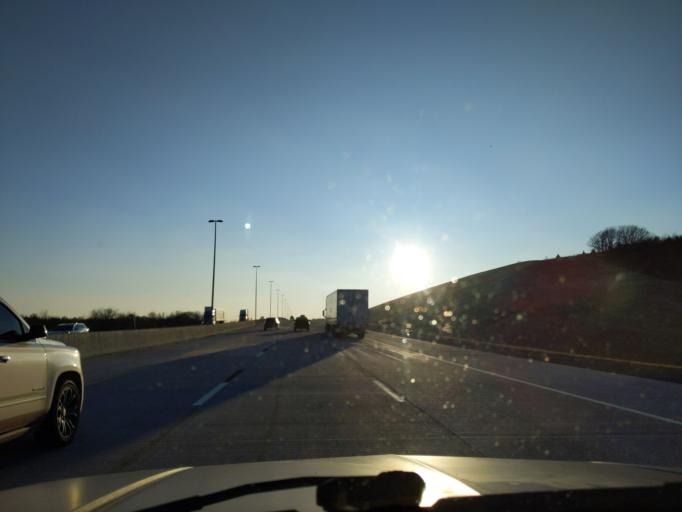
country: US
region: Oklahoma
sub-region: Creek County
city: Kellyville
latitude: 35.9766
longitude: -96.2093
